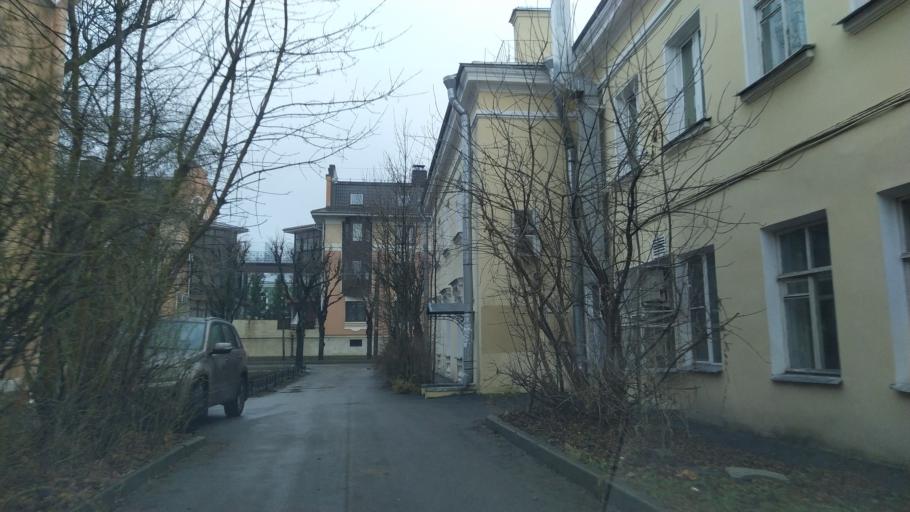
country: RU
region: St.-Petersburg
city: Pushkin
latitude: 59.7205
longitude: 30.4166
